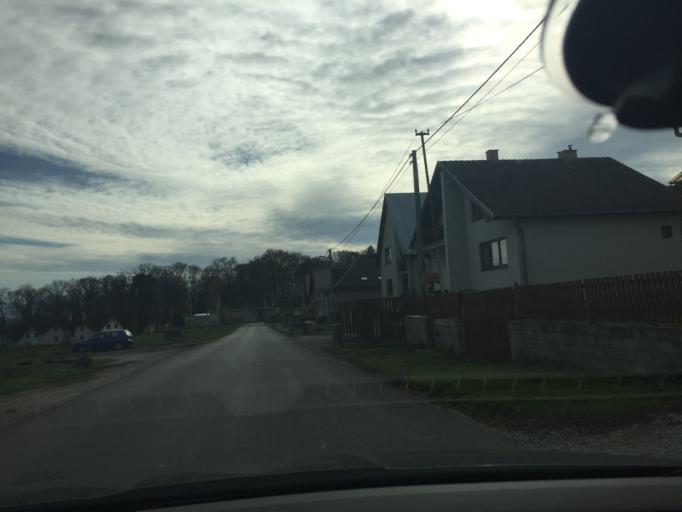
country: SK
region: Presovsky
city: Spisske Podhradie
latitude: 48.9919
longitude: 20.7807
